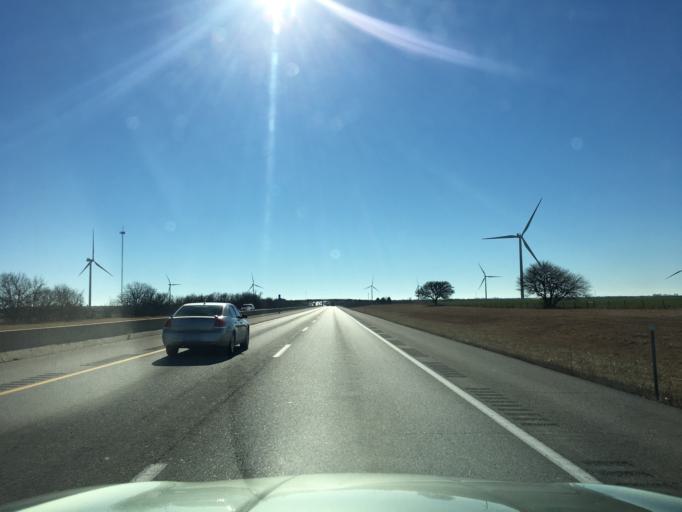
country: US
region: Kansas
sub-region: Sumner County
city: Wellington
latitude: 37.1503
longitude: -97.3395
